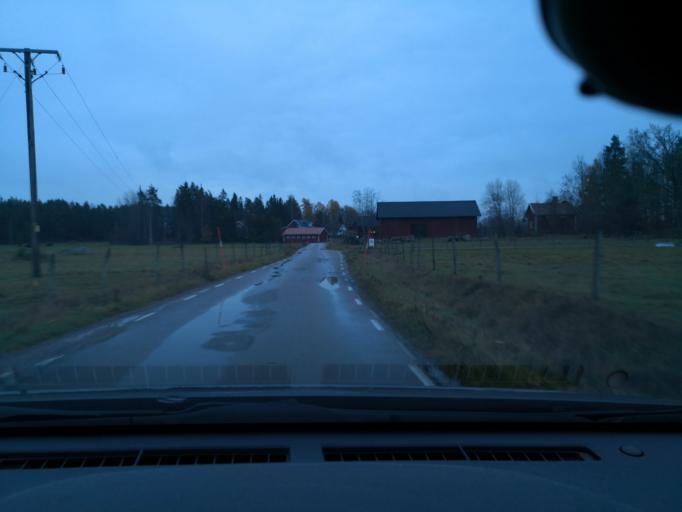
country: SE
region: Vaestmanland
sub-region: Hallstahammars Kommun
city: Kolback
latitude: 59.5679
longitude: 16.1925
